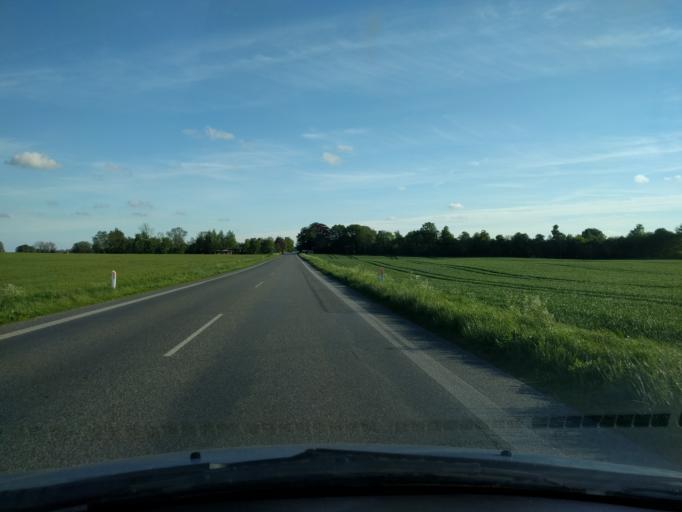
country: DK
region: Zealand
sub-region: Guldborgsund Kommune
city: Stubbekobing
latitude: 54.8685
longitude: 12.0227
